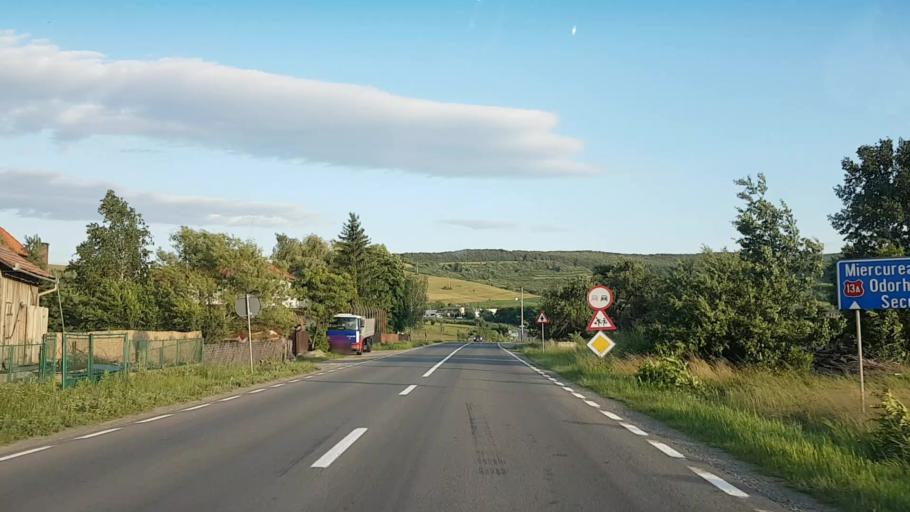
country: RO
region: Harghita
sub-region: Comuna Lupeni
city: Lupeni
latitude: 46.3610
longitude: 25.2378
